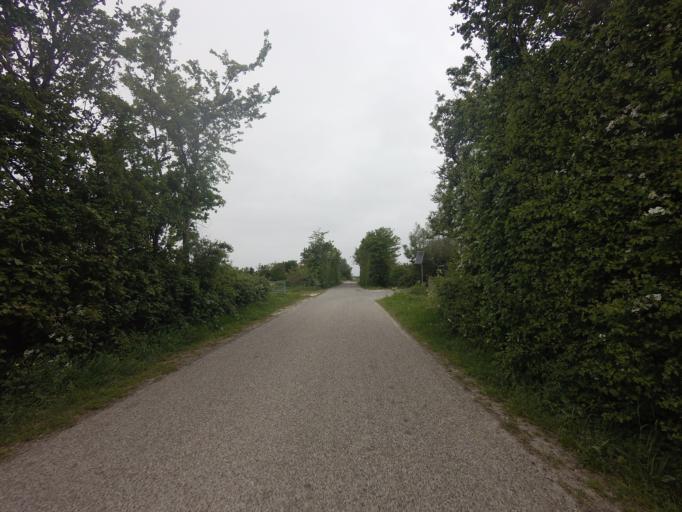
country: NL
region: Zeeland
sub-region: Gemeente Middelburg
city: Middelburg
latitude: 51.5541
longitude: 3.5687
